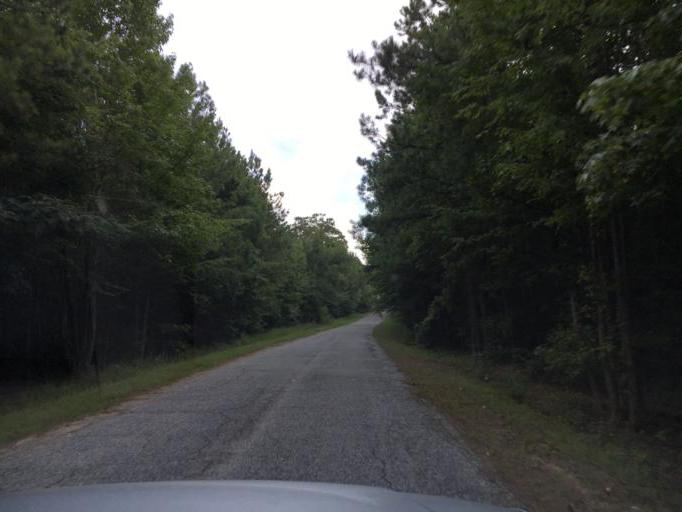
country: US
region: South Carolina
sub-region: Laurens County
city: Watts Mills
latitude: 34.5379
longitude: -81.9412
